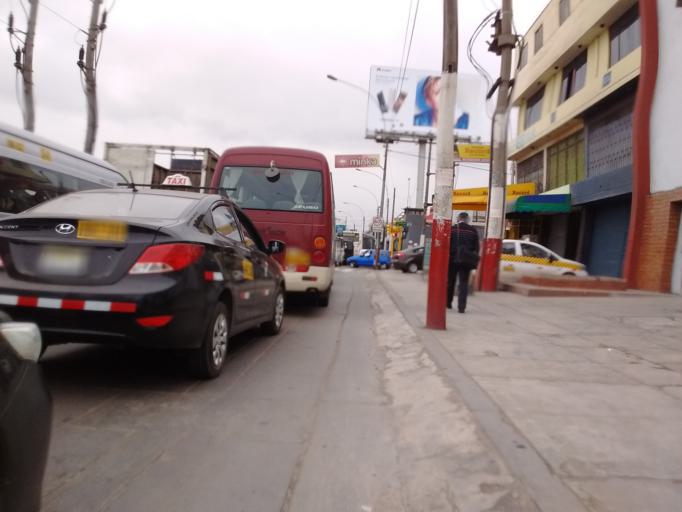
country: PE
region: Callao
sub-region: Callao
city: Callao
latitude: -12.0501
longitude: -77.0982
